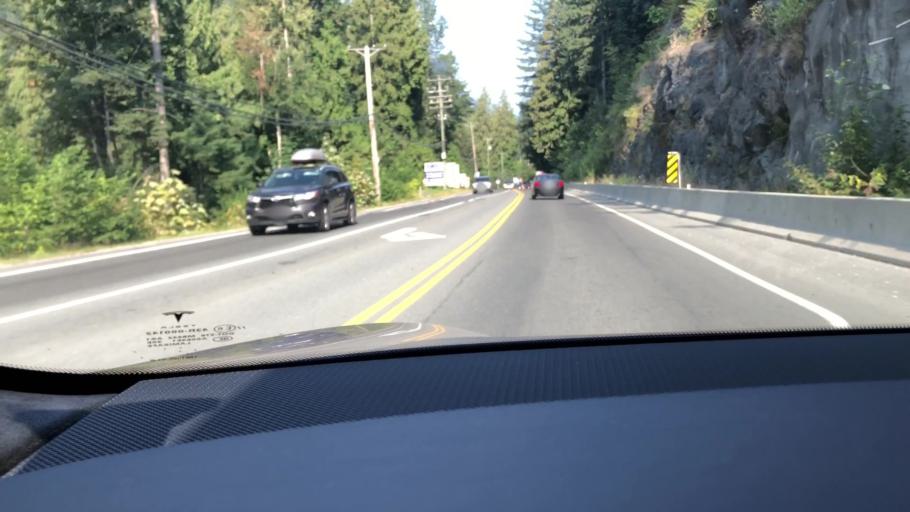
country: CA
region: British Columbia
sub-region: Fraser Valley Regional District
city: Chilliwack
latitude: 49.0923
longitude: -121.9687
